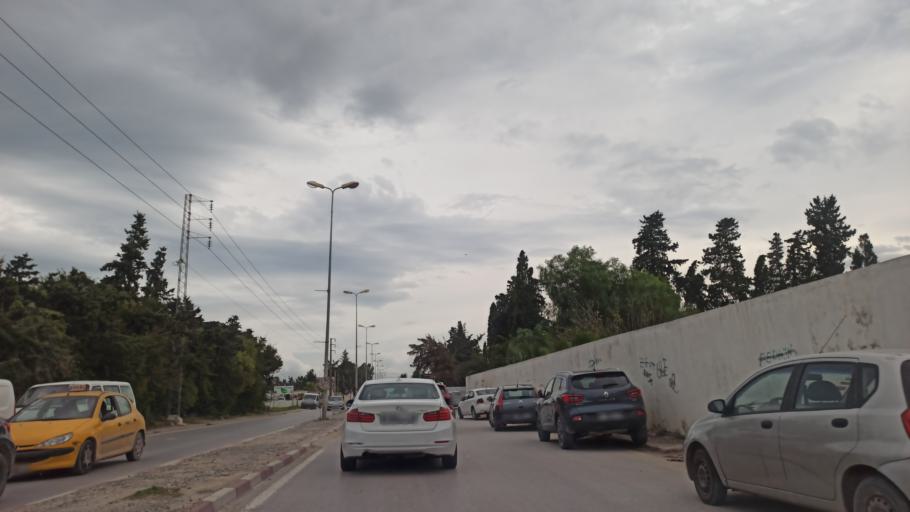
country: TN
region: Ariana
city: Ariana
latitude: 36.8740
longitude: 10.2463
